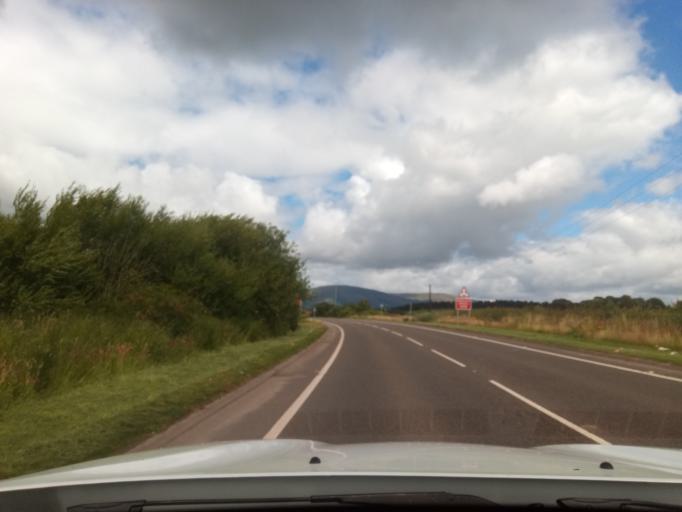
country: GB
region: Scotland
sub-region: Fife
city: Kincardine
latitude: 56.0944
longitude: -3.7178
